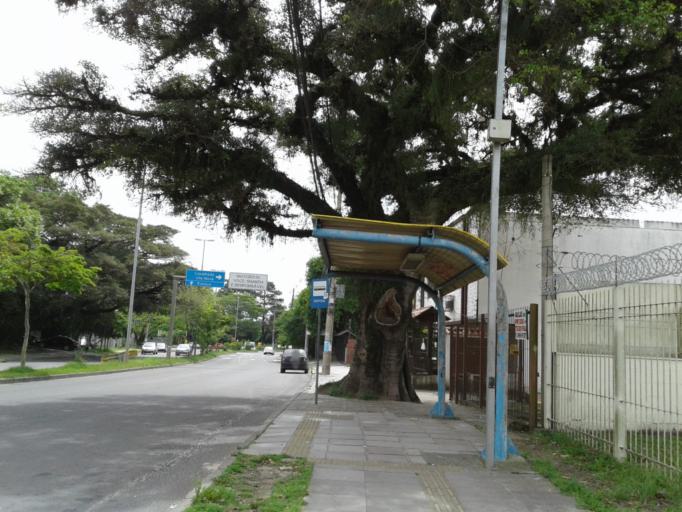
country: BR
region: Rio Grande do Sul
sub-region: Porto Alegre
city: Porto Alegre
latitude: -30.1356
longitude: -51.2232
